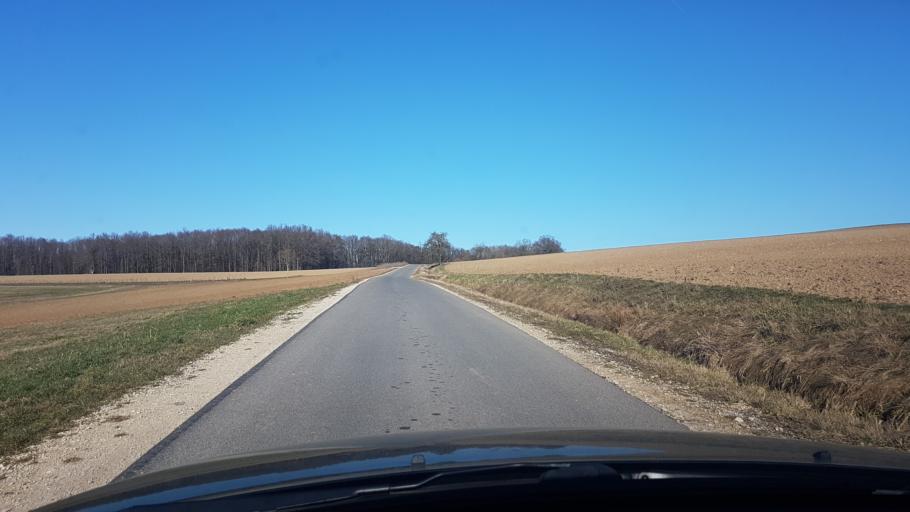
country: DE
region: Bavaria
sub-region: Upper Franconia
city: Zapfendorf
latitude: 50.0167
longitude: 10.9844
